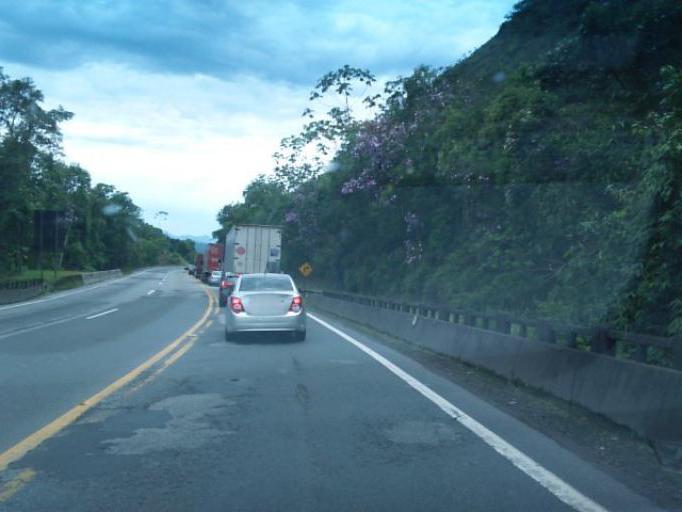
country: BR
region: Sao Paulo
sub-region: Juquitiba
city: Juquitiba
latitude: -24.1058
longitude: -47.2636
